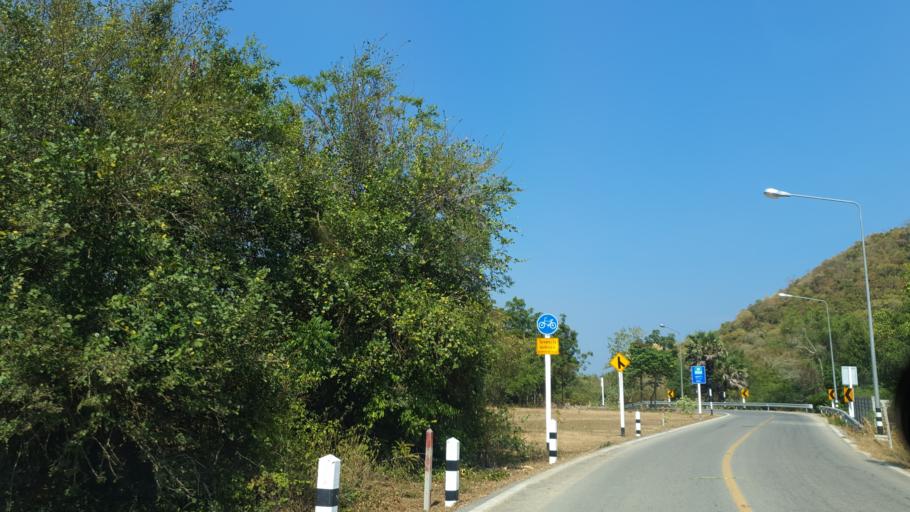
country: TH
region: Prachuap Khiri Khan
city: Sam Roi Yot
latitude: 12.2781
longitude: 99.9733
